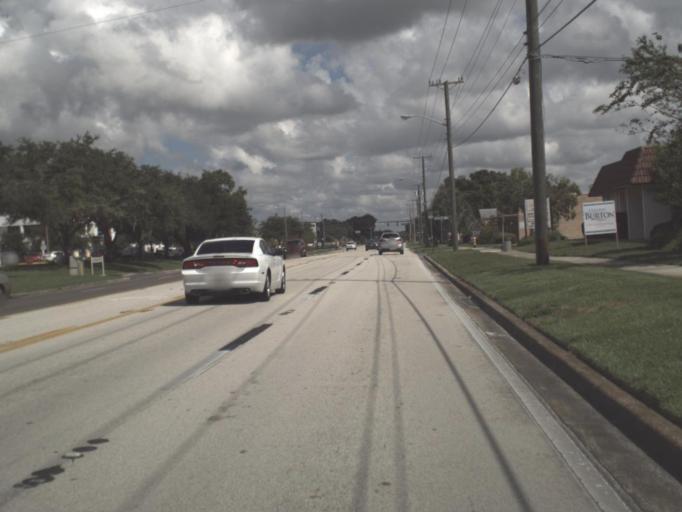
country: US
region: Florida
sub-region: Polk County
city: Lakeland
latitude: 28.0673
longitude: -81.9532
